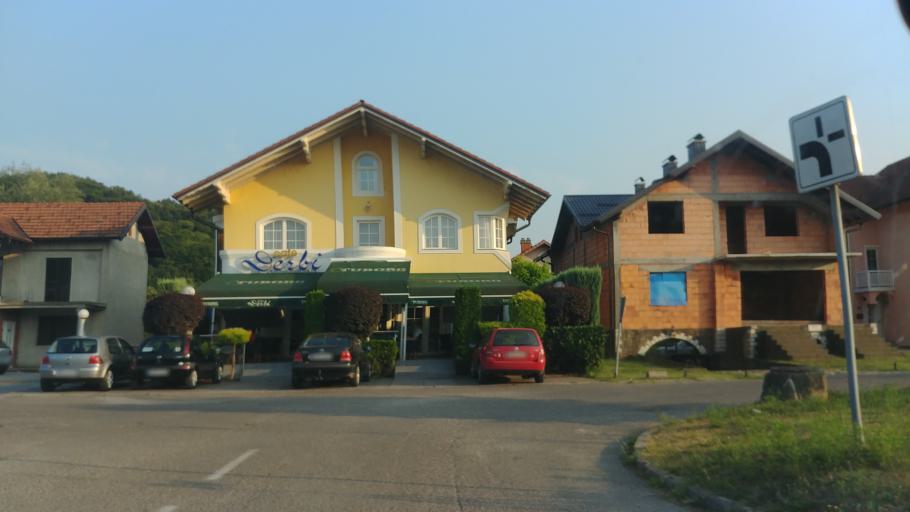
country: BA
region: Republika Srpska
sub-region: Opstina Ugljevik
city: Ugljevik
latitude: 44.6911
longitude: 18.9960
